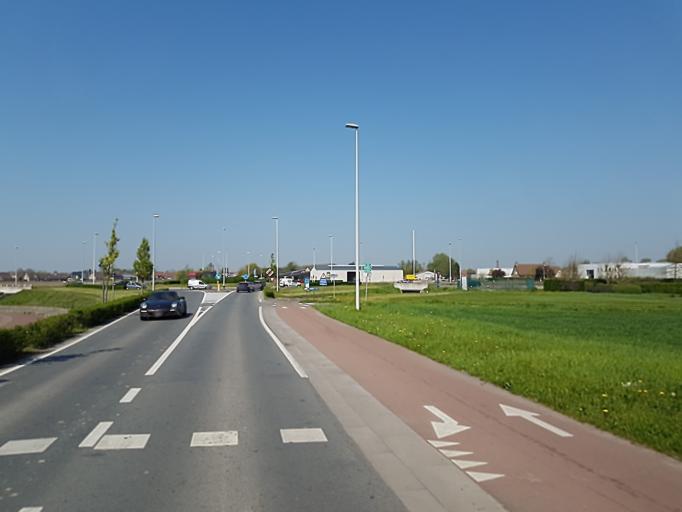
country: BE
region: Flanders
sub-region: Provincie West-Vlaanderen
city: Menen
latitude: 50.8061
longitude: 3.0907
